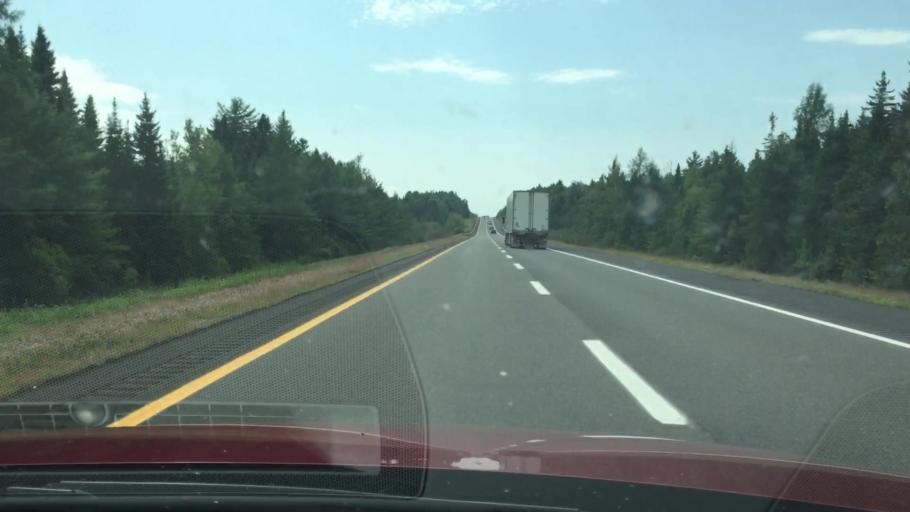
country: US
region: Maine
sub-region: Penobscot County
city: Patten
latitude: 46.0672
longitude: -68.2275
